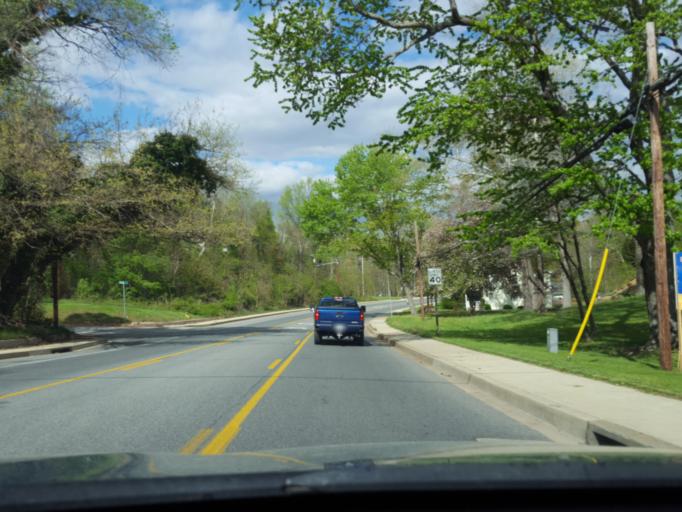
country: US
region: Maryland
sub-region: Charles County
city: La Plata
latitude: 38.5311
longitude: -76.9707
